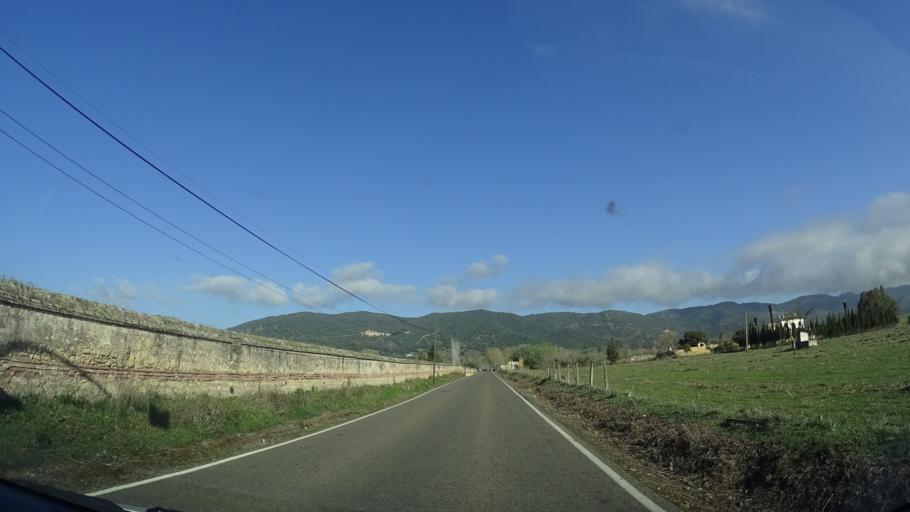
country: ES
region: Andalusia
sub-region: Province of Cordoba
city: Villarrubia
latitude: 37.8772
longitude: -4.8498
